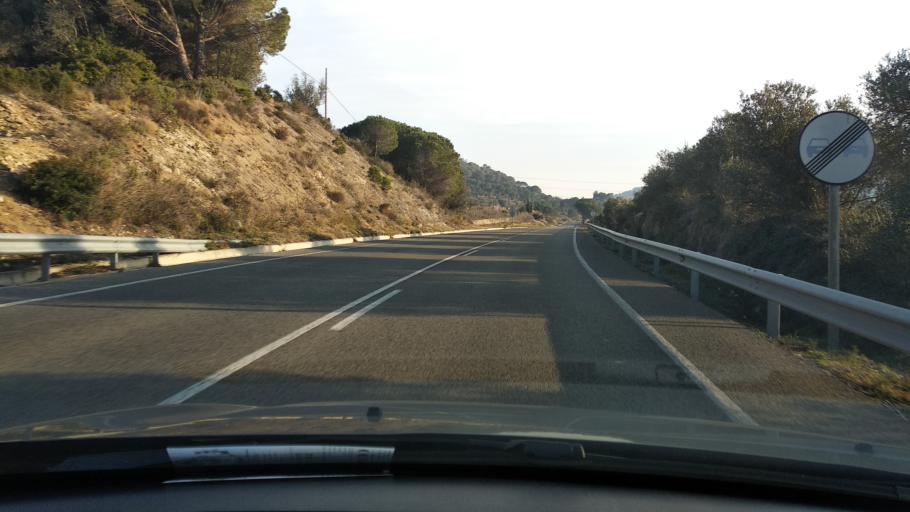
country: ES
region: Catalonia
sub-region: Provincia de Tarragona
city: Alforja
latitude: 41.2025
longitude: 0.9960
